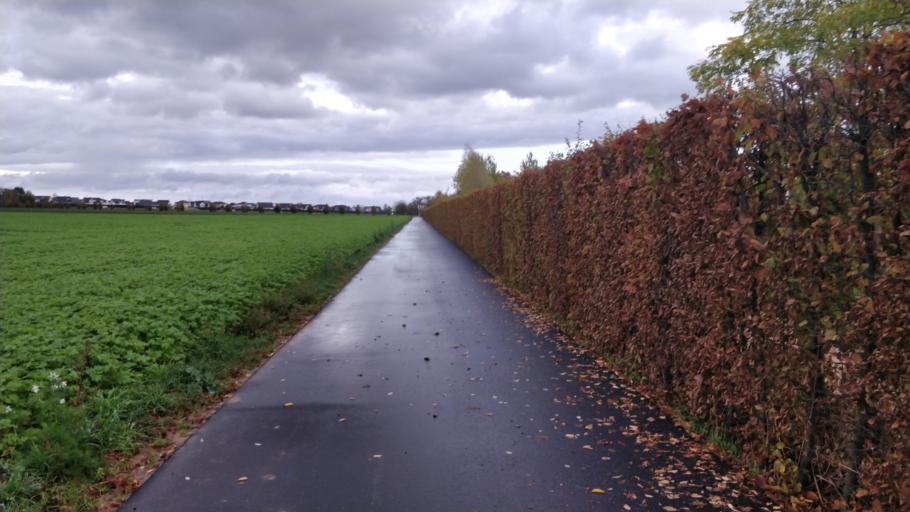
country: DE
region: North Rhine-Westphalia
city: Zulpich
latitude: 50.6816
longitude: 6.6541
